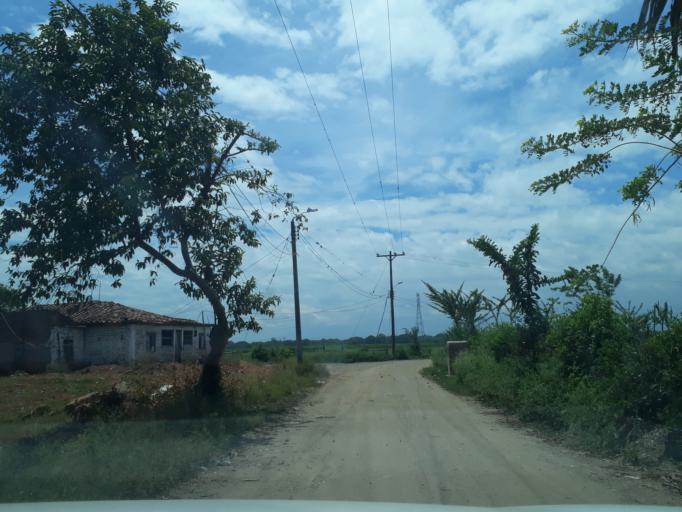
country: CO
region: Valle del Cauca
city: Cali
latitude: 3.3670
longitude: -76.4794
